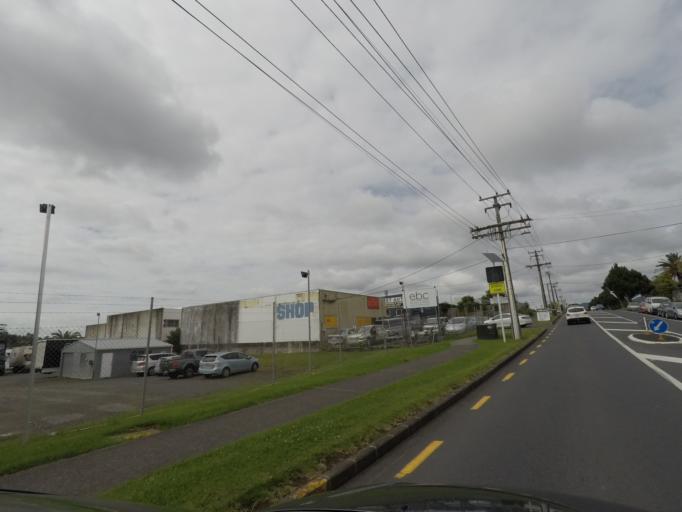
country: NZ
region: Auckland
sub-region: Auckland
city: Waitakere
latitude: -36.8943
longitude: 174.6285
